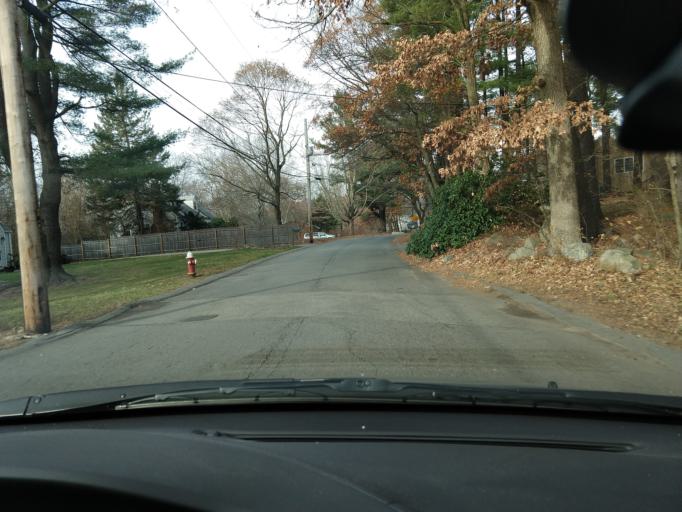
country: US
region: Massachusetts
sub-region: Middlesex County
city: Bedford
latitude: 42.4810
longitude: -71.2597
